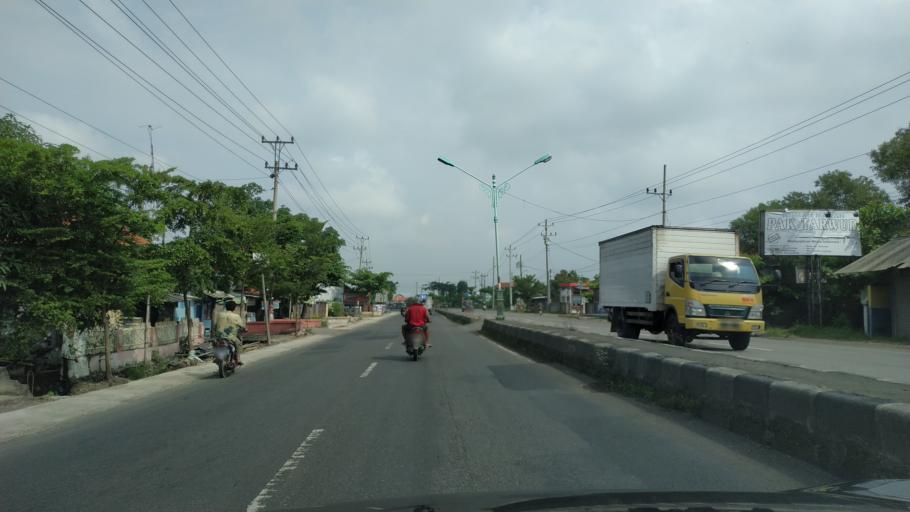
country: ID
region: Central Java
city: Bulakamba
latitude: -6.8731
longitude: 108.9123
